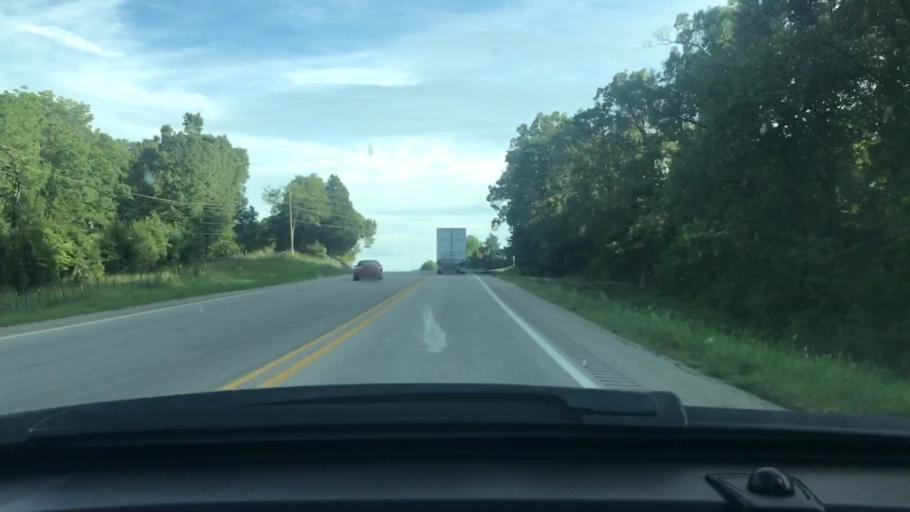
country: US
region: Arkansas
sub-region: Lawrence County
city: Hoxie
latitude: 36.1567
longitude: -91.1618
